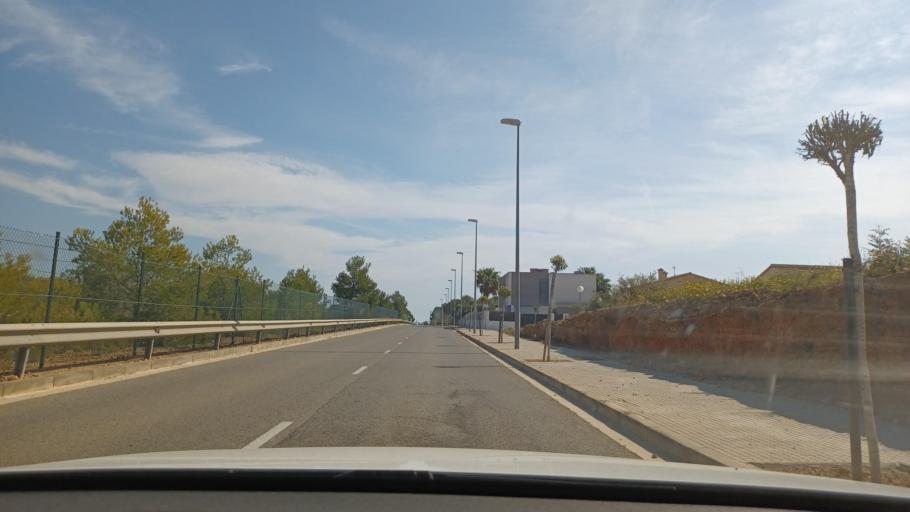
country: ES
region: Catalonia
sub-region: Provincia de Tarragona
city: L'Ampolla
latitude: 40.8224
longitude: 0.7260
